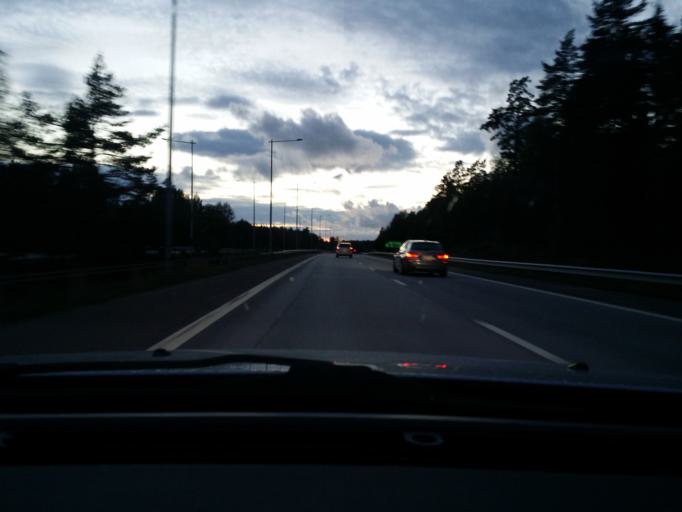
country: SE
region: Stockholm
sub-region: Upplands-Bro Kommun
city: Bro
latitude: 59.5256
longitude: 17.6472
